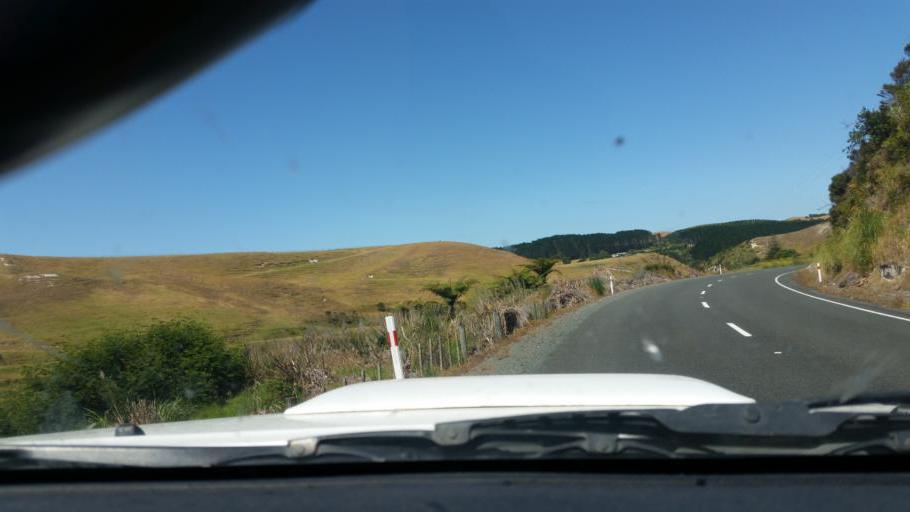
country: NZ
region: Northland
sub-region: Kaipara District
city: Dargaville
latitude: -35.8309
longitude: 173.6674
